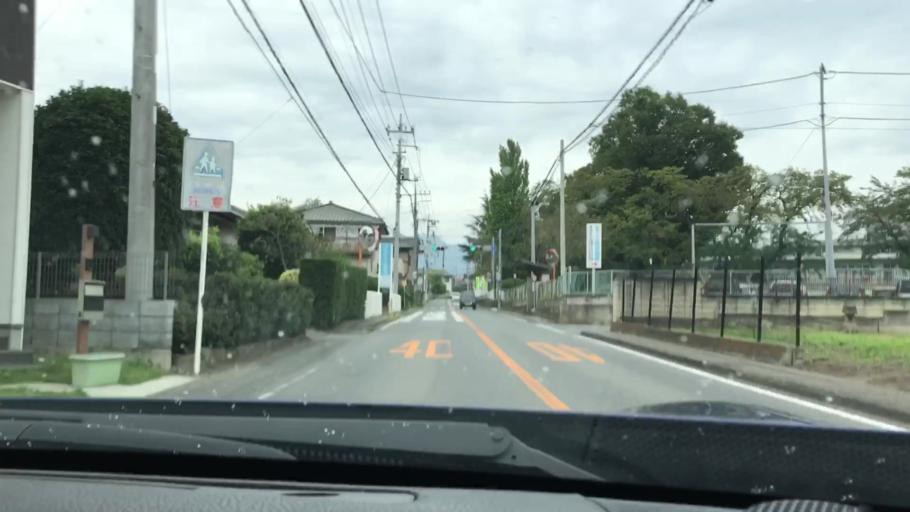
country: JP
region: Gunma
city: Kanekomachi
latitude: 36.3868
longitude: 138.9833
